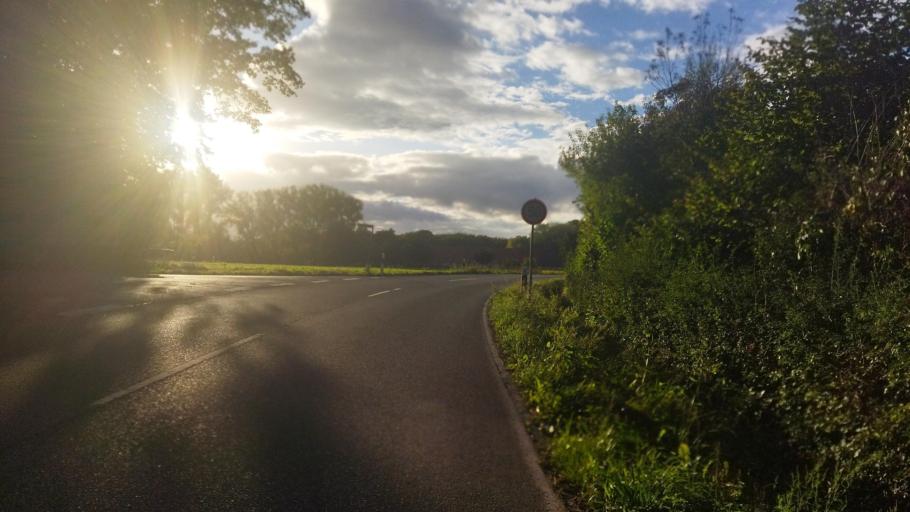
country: DE
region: North Rhine-Westphalia
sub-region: Regierungsbezirk Munster
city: Billerbeck
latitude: 51.9708
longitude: 7.2537
